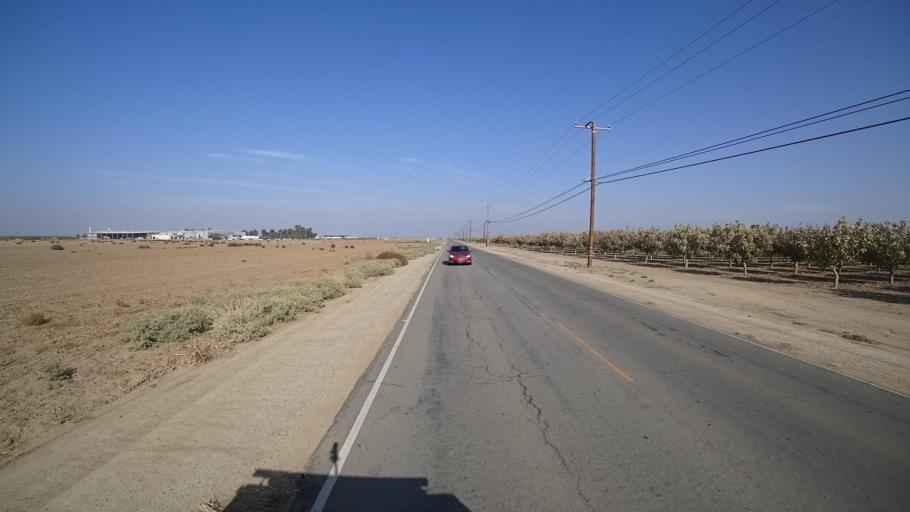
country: US
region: California
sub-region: Kern County
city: McFarland
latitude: 35.6983
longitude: -119.2238
